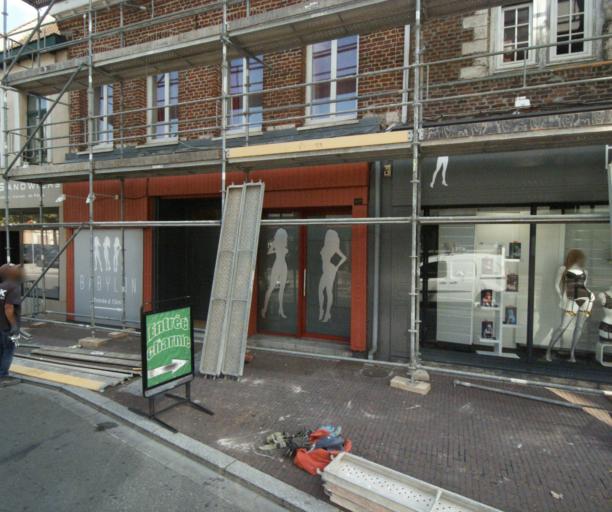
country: FR
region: Nord-Pas-de-Calais
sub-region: Departement du Nord
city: Tourcoing
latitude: 50.7217
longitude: 3.1611
